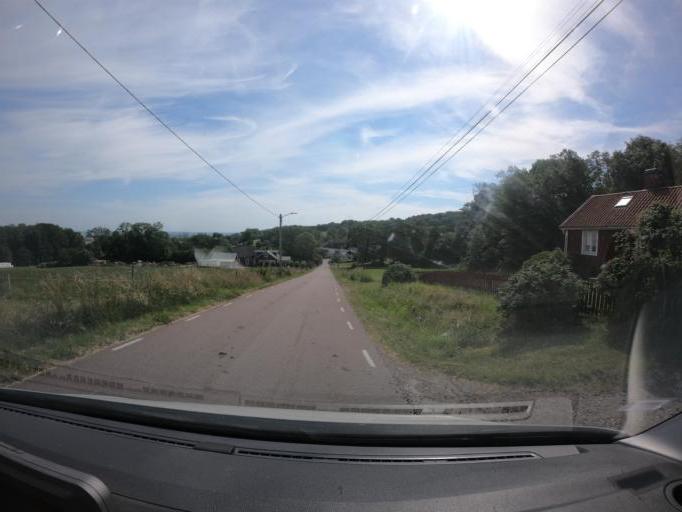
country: SE
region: Skane
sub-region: Bastads Kommun
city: Bastad
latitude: 56.4169
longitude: 12.9415
